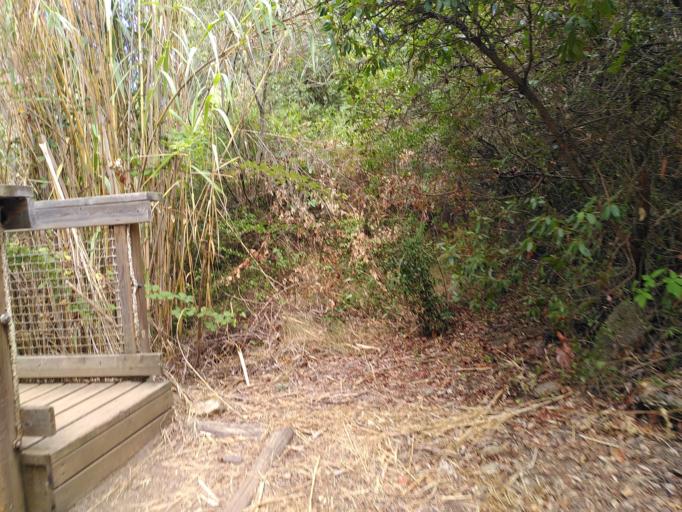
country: FR
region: Provence-Alpes-Cote d'Azur
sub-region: Departement du Var
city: Cavalaire-sur-Mer
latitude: 43.1657
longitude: 6.5133
